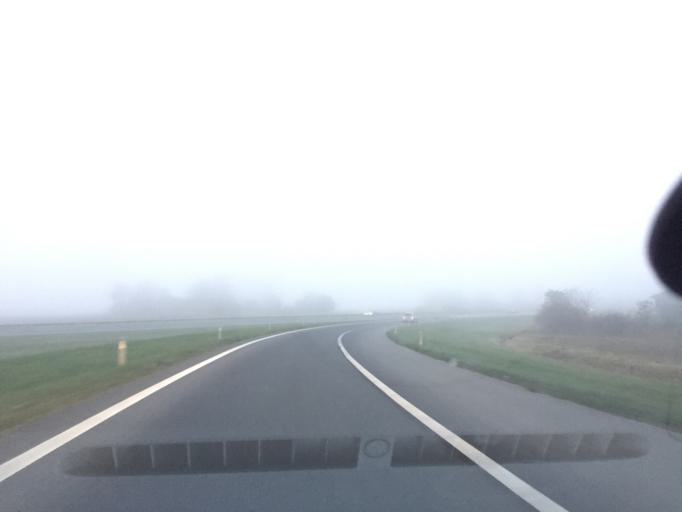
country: NL
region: Gelderland
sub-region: Gemeente Doetinchem
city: Doetinchem
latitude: 51.9441
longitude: 6.2700
